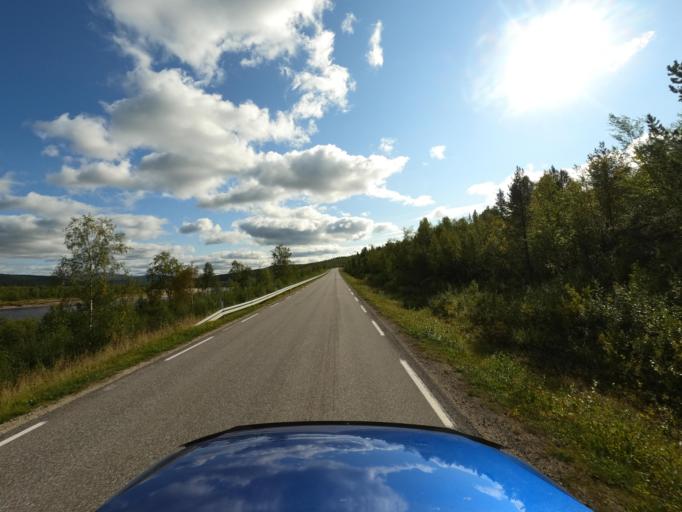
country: NO
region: Finnmark Fylke
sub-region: Karasjok
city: Karasjohka
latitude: 69.4440
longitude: 25.6315
